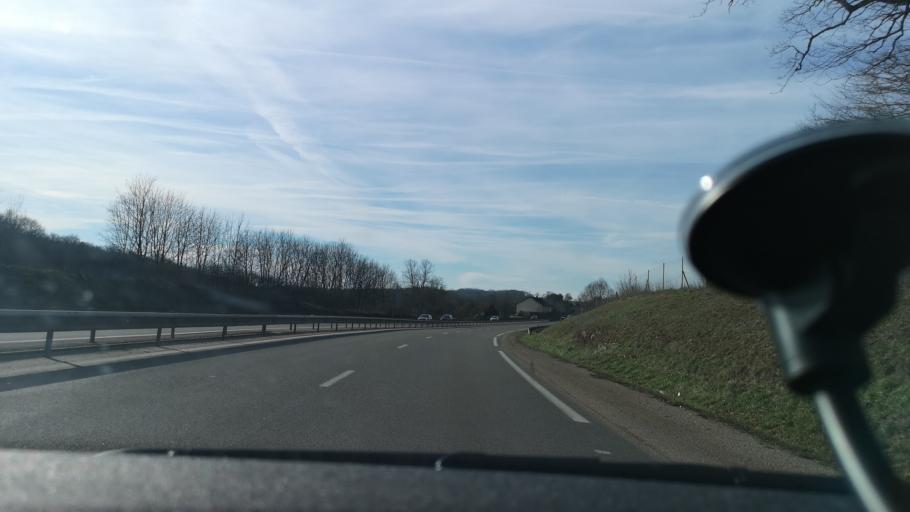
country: FR
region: Franche-Comte
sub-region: Departement du Doubs
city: Grandfontaine
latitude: 47.2096
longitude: 5.9089
